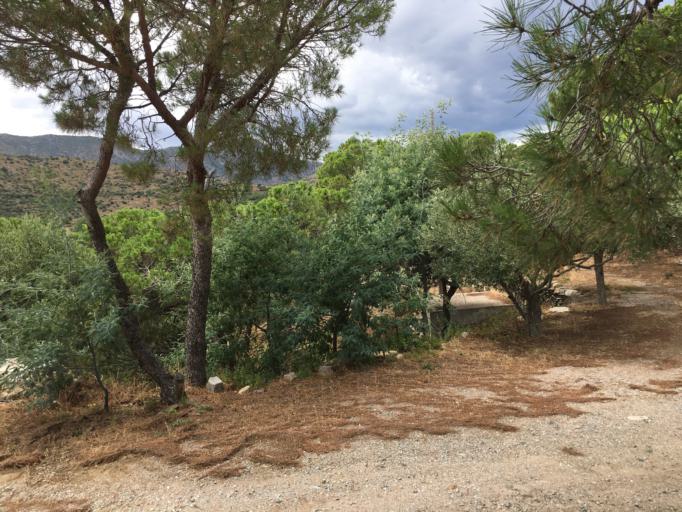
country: ES
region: Catalonia
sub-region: Provincia de Girona
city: Roses
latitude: 42.3116
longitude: 3.2163
